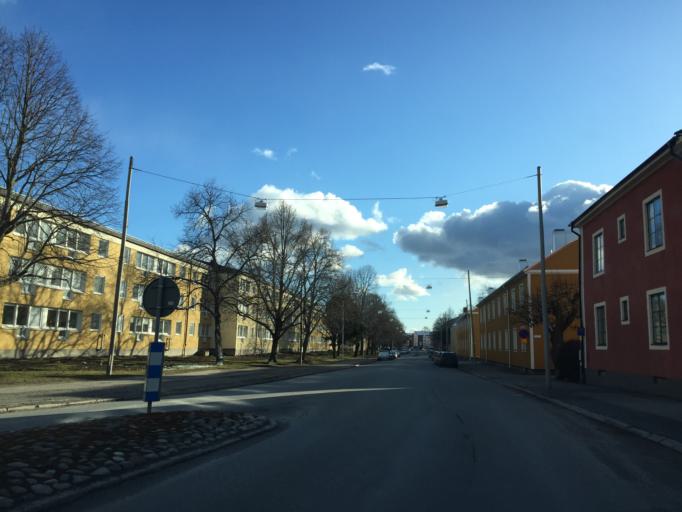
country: SE
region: OErebro
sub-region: Orebro Kommun
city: Orebro
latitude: 59.2833
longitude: 15.2125
